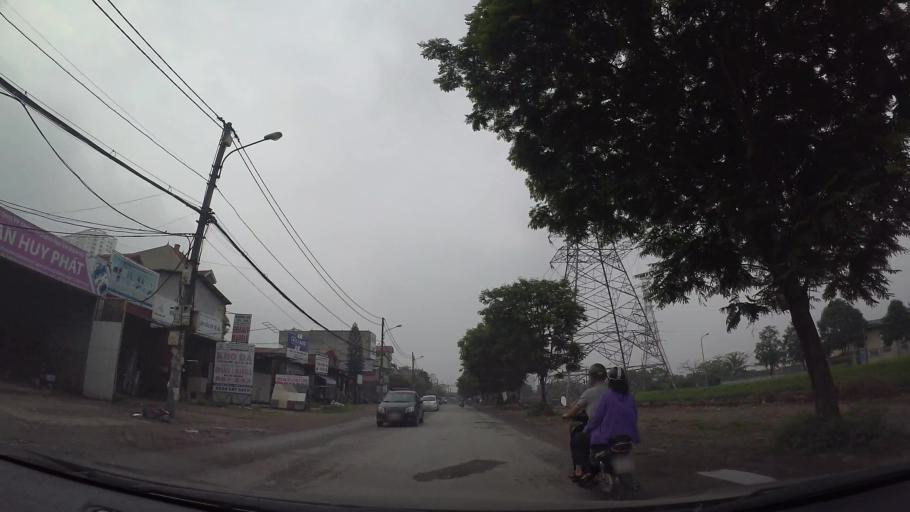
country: VN
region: Ha Noi
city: Van Dien
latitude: 20.9775
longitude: 105.8653
